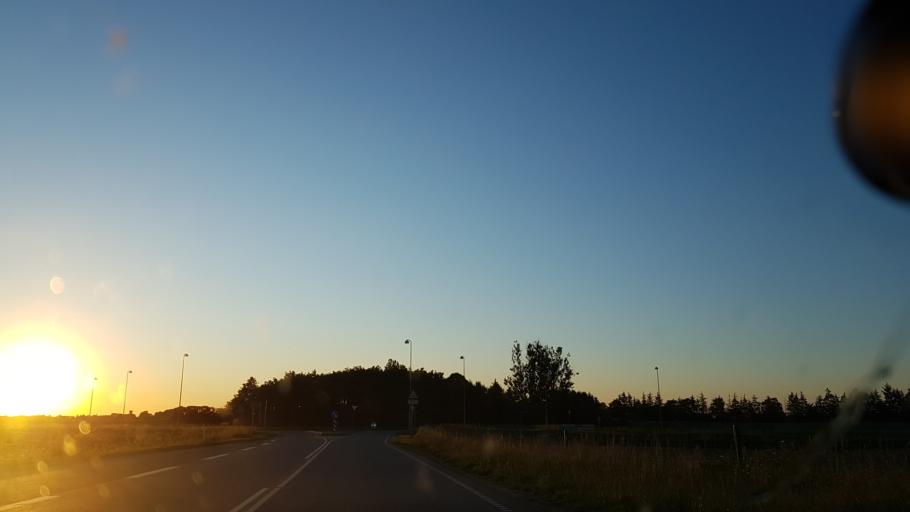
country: DK
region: South Denmark
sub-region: Aabenraa Kommune
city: Krusa
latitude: 54.9385
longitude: 9.3635
